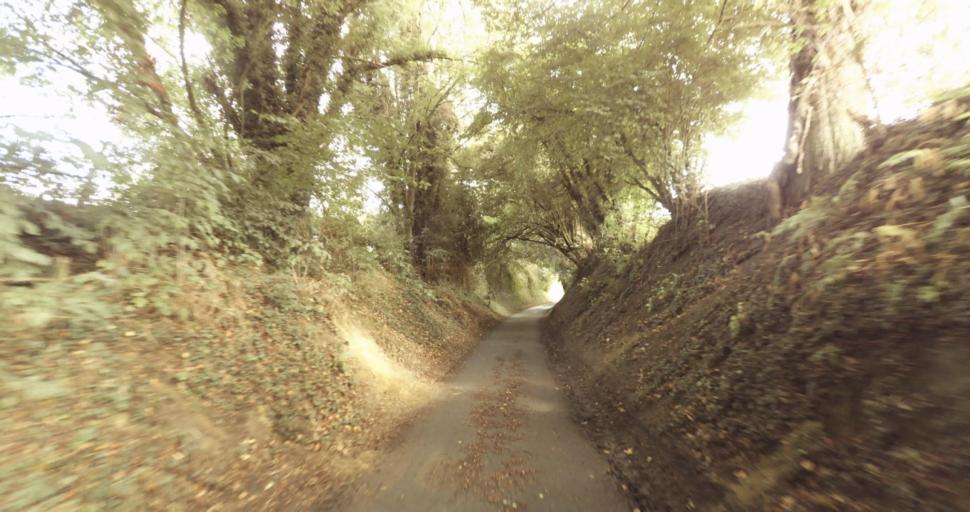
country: FR
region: Lower Normandy
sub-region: Departement de l'Orne
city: Vimoutiers
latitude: 48.8590
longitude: 0.1550
